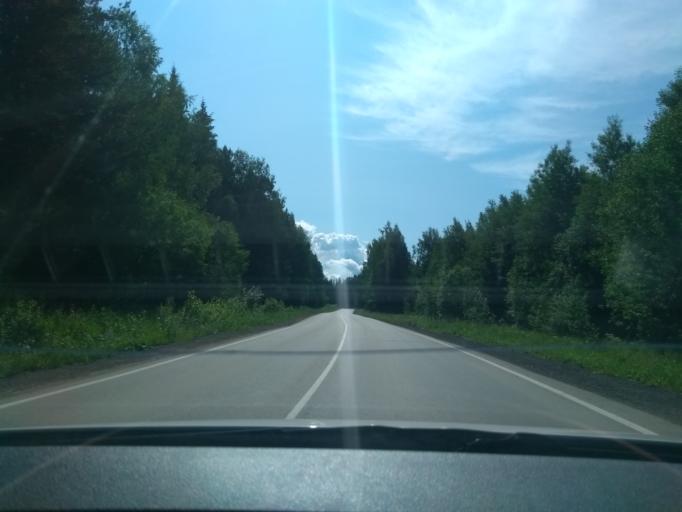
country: RU
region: Perm
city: Bershet'
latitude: 57.8303
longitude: 56.4067
